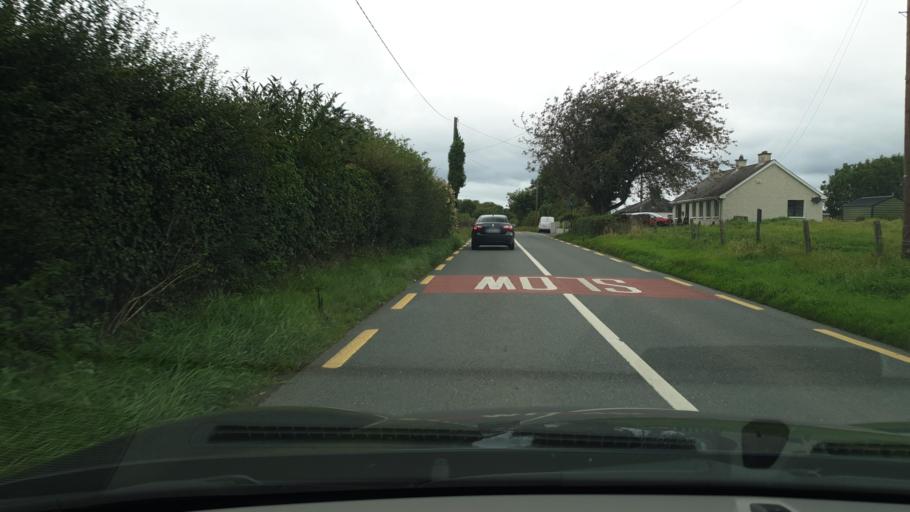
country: IE
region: Leinster
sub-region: Kildare
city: Clane
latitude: 53.2778
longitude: -6.6968
